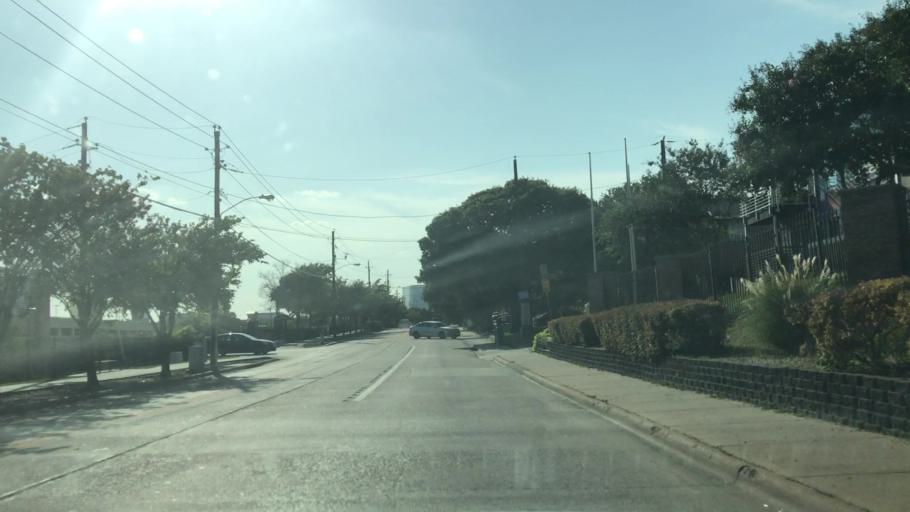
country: US
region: Texas
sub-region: Dallas County
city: University Park
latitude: 32.8642
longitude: -96.7522
